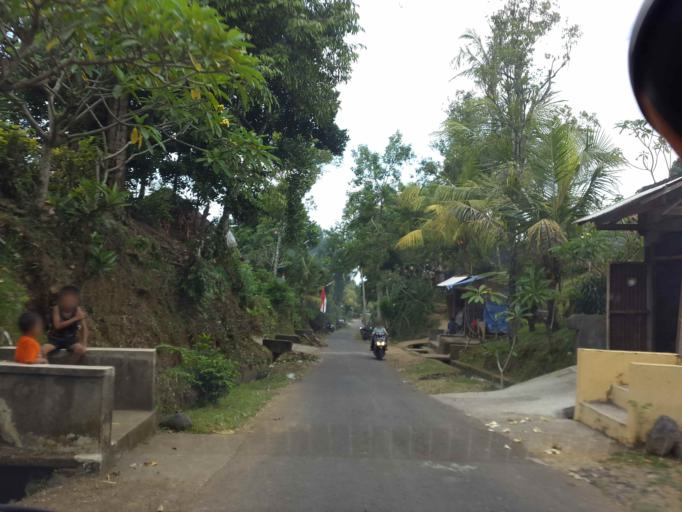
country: ID
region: Bali
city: Banjar Kelodan
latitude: -8.4974
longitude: 115.3693
